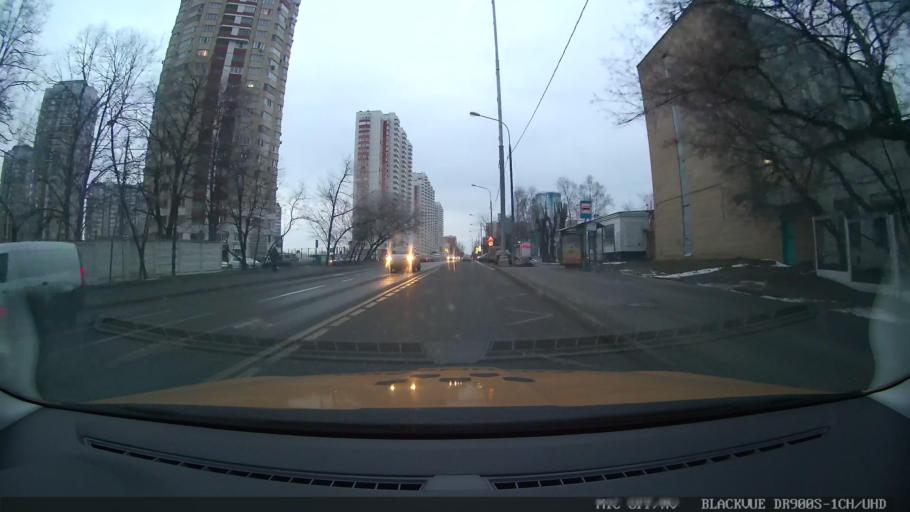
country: RU
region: Moscow
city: Amin'yevo
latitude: 55.6920
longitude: 37.4691
